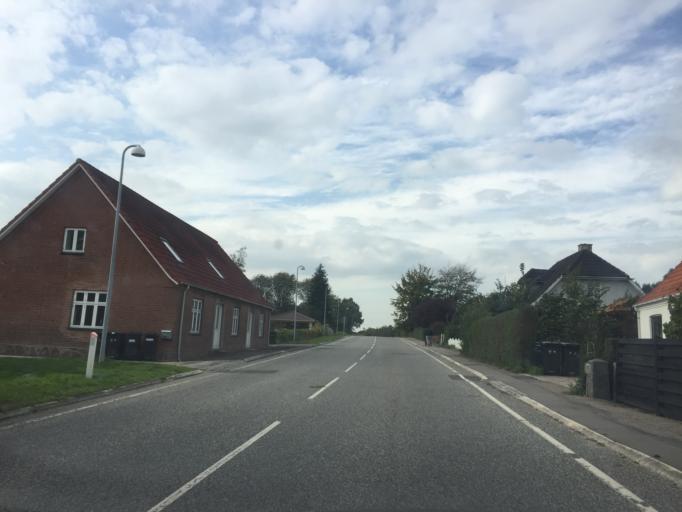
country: DK
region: Zealand
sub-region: Vordingborg Kommune
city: Praesto
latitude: 55.1639
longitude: 11.9745
